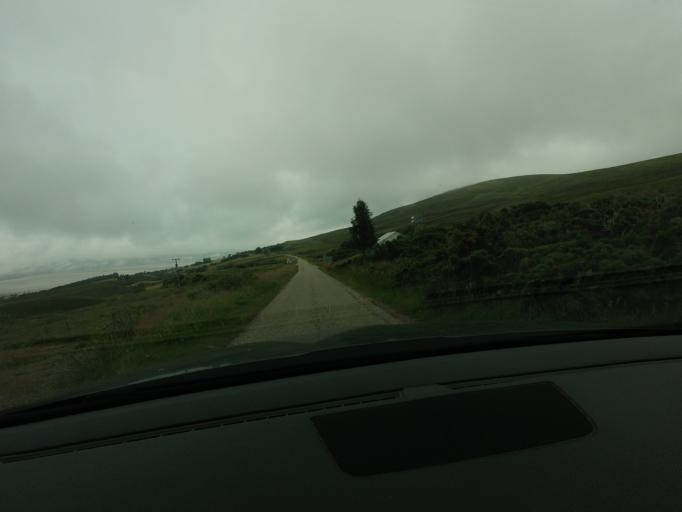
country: GB
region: Scotland
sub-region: Highland
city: Golspie
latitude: 58.4696
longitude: -4.4022
